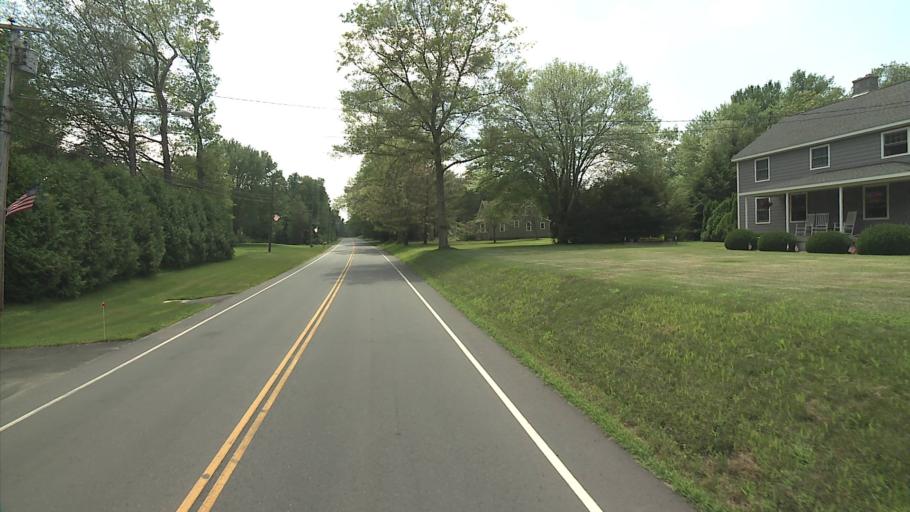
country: US
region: Connecticut
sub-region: New London County
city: Preston City
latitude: 41.5674
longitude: -71.8679
